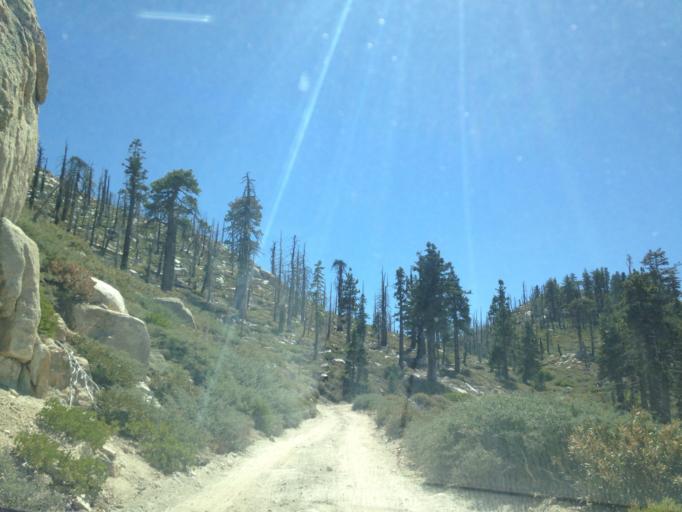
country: US
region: California
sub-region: San Bernardino County
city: Big Bear Lake
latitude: 34.2595
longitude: -116.9985
